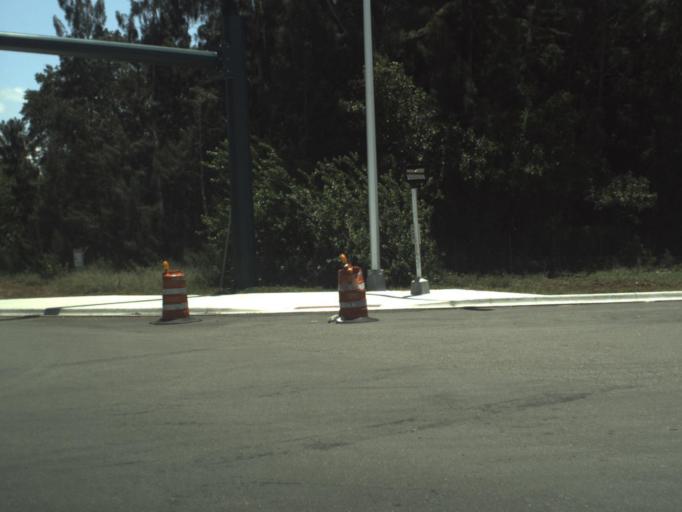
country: US
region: Florida
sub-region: Martin County
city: Palm City
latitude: 27.1613
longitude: -80.3006
